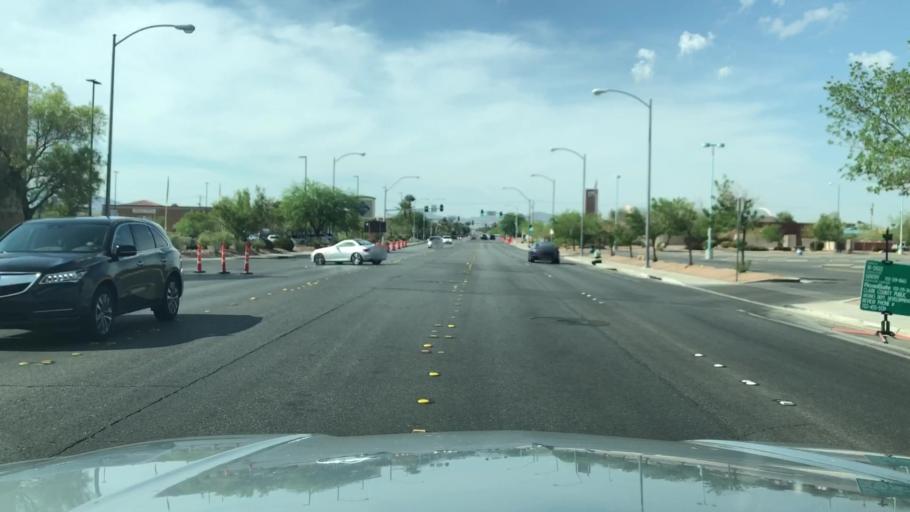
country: US
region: Nevada
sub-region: Clark County
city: Whitney
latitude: 36.0235
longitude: -115.1275
